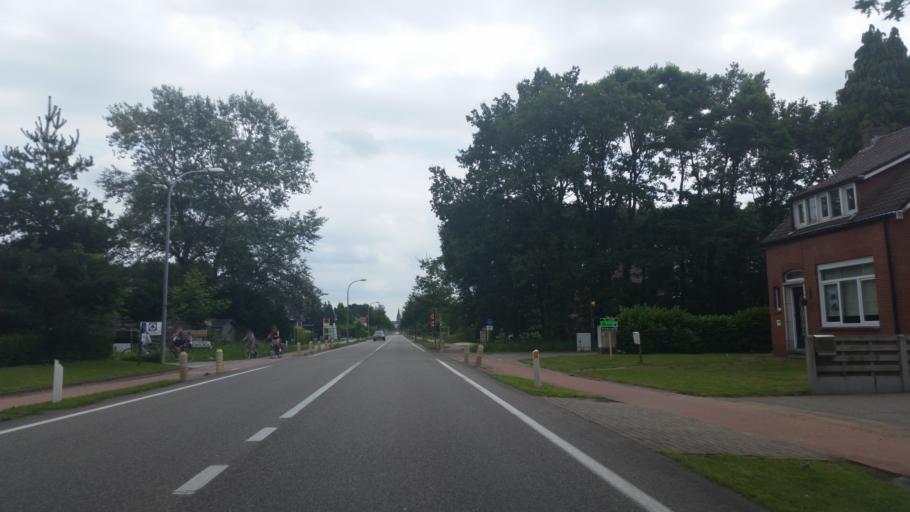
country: BE
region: Flanders
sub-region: Provincie Antwerpen
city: Merksplas
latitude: 51.3676
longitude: 4.8482
